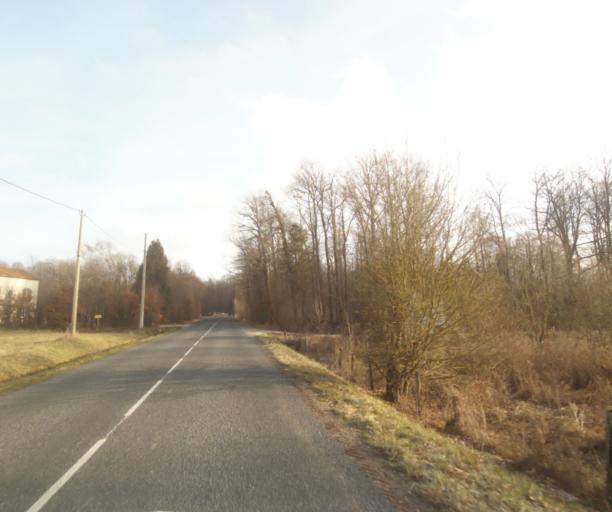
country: FR
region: Champagne-Ardenne
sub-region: Departement de la Haute-Marne
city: Saint-Dizier
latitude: 48.6607
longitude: 4.9435
